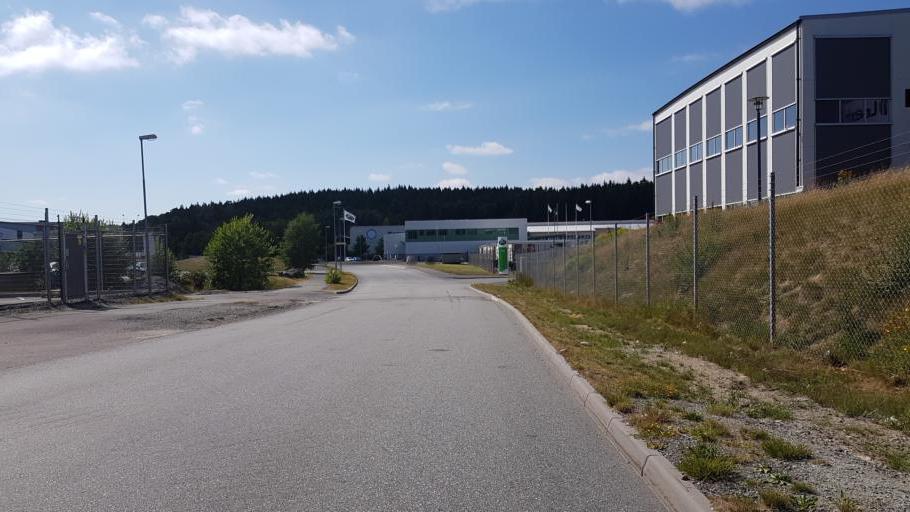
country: SE
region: Vaestra Goetaland
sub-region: Harryda Kommun
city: Molnlycke
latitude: 57.6758
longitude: 12.0908
